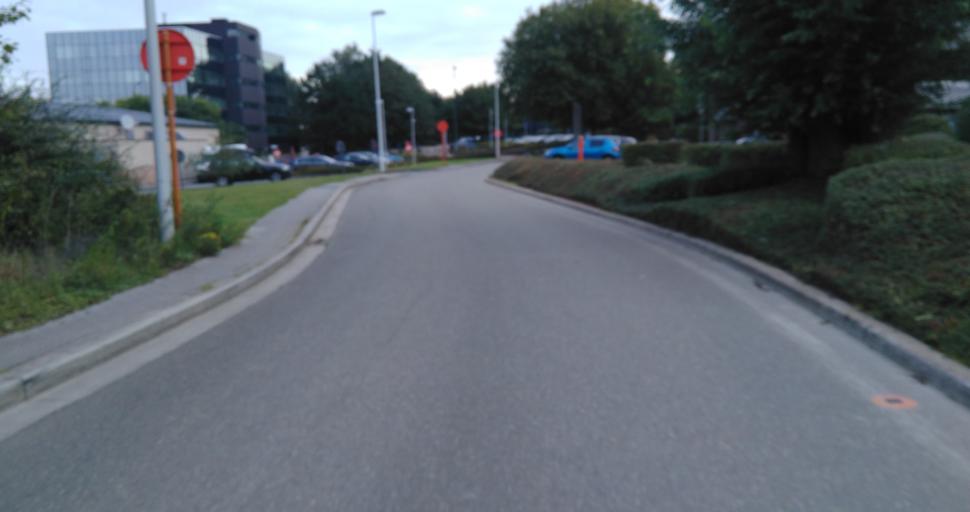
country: BE
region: Flanders
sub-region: Provincie Vlaams-Brabant
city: Zaventem
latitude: 50.8802
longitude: 4.4501
